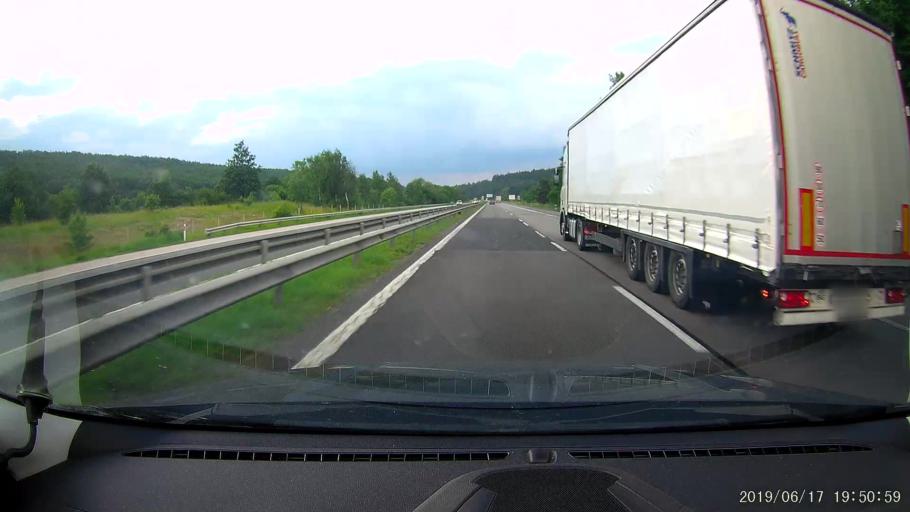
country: BG
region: Sofiya
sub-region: Obshtina Ikhtiman
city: Ikhtiman
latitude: 42.5025
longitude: 23.7693
